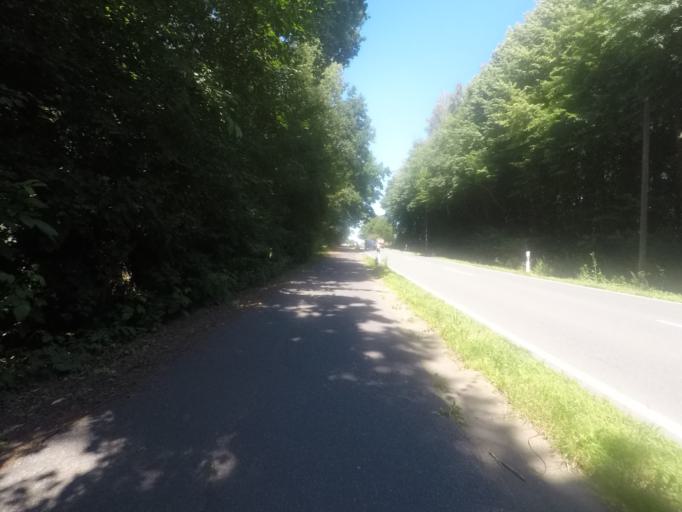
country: DE
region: North Rhine-Westphalia
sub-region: Regierungsbezirk Detmold
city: Bielefeld
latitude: 52.0604
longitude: 8.5269
